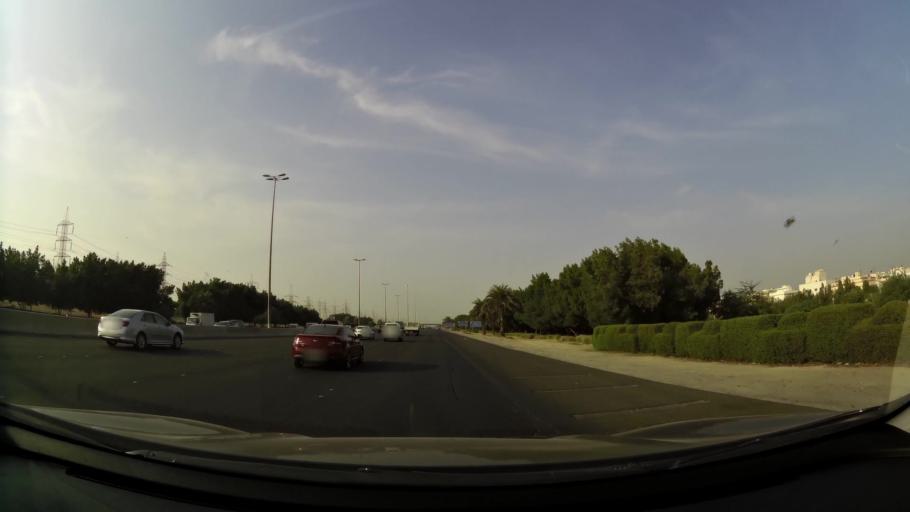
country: KW
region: Mubarak al Kabir
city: Mubarak al Kabir
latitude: 29.1996
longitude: 48.0618
